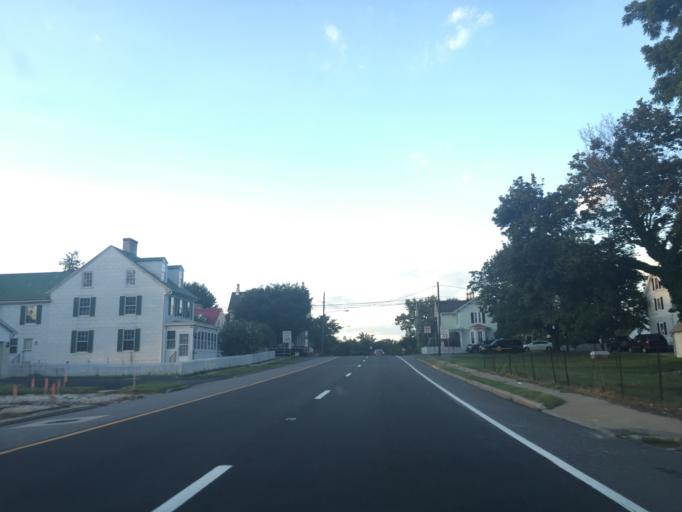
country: US
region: Delaware
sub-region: New Castle County
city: Middletown
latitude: 39.4566
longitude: -75.6605
